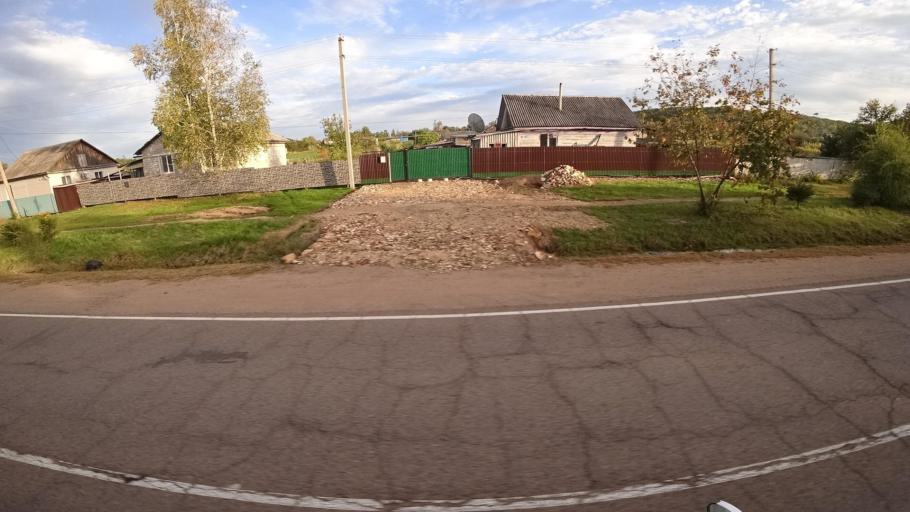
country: RU
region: Primorskiy
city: Yakovlevka
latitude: 44.4242
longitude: 133.4659
